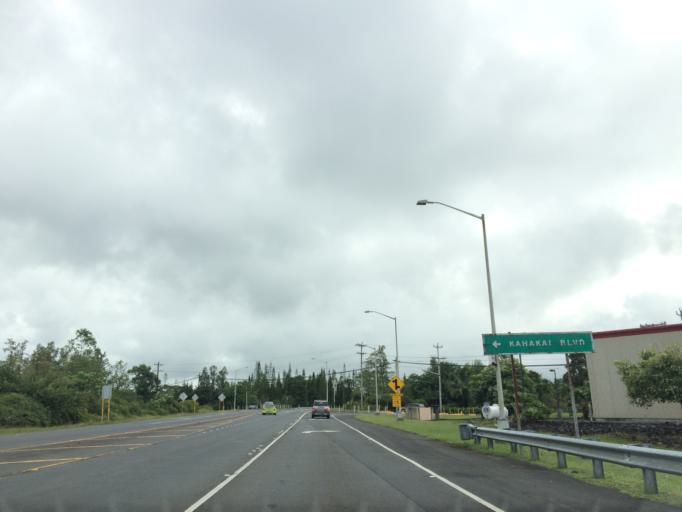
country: US
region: Hawaii
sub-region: Hawaii County
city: Hawaiian Paradise Park
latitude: 19.5048
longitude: -154.9545
